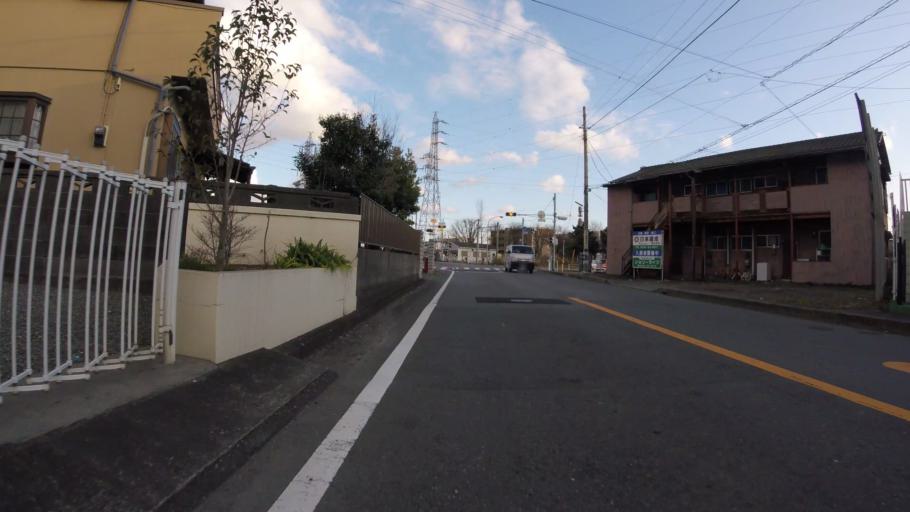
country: JP
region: Shizuoka
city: Fuji
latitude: 35.1551
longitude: 138.6919
